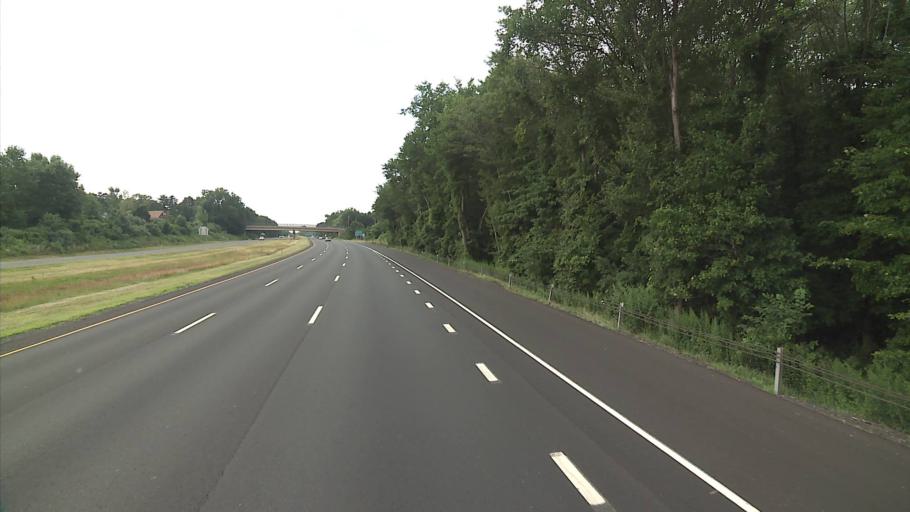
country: US
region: Connecticut
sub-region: Hartford County
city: Plainville
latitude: 41.6092
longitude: -72.9011
